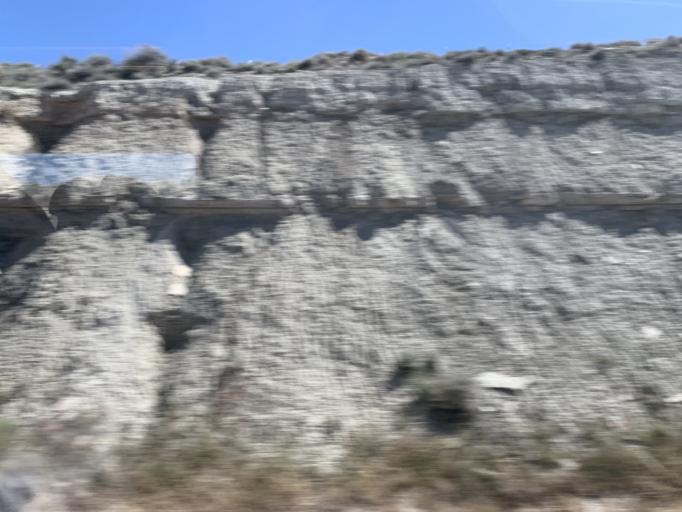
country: ES
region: Aragon
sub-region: Provincia de Huesca
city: Penalba
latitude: 41.5278
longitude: -0.0724
